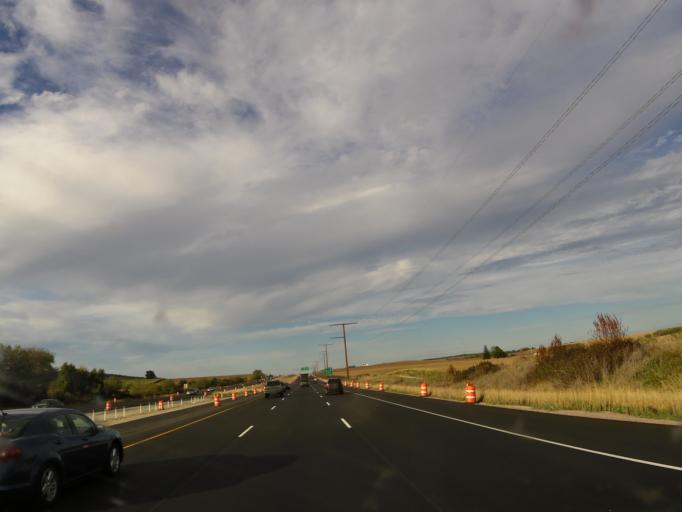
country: US
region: Wisconsin
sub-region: Columbia County
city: Portage
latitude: 43.4628
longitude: -89.4966
